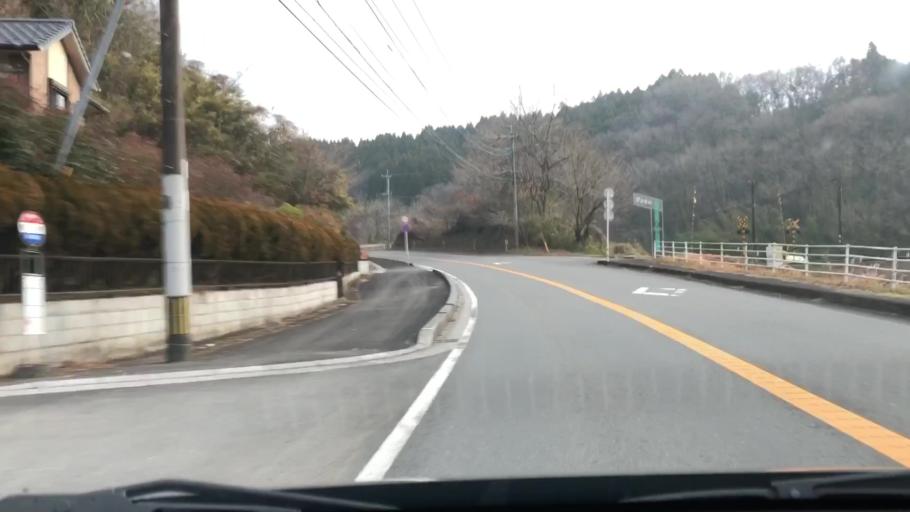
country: JP
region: Oita
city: Takedamachi
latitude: 32.9744
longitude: 131.5281
